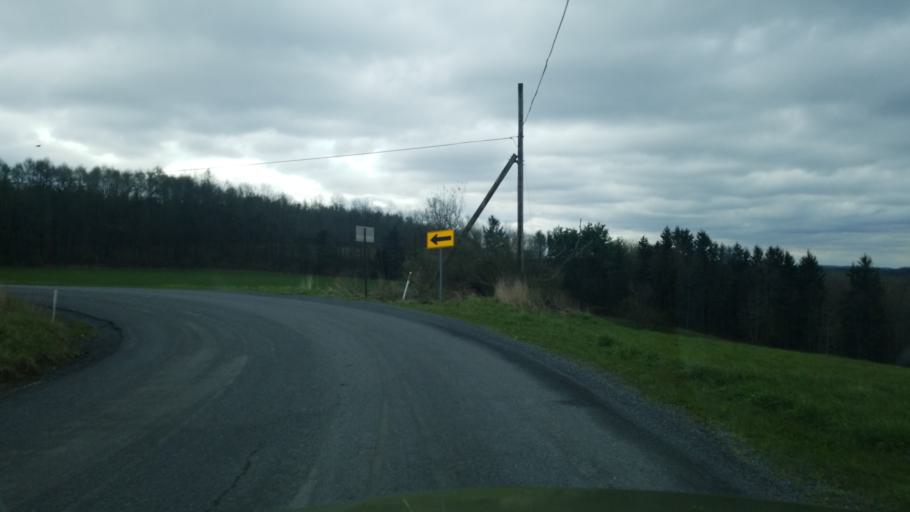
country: US
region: Pennsylvania
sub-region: Clearfield County
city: Clearfield
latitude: 41.0812
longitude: -78.3964
